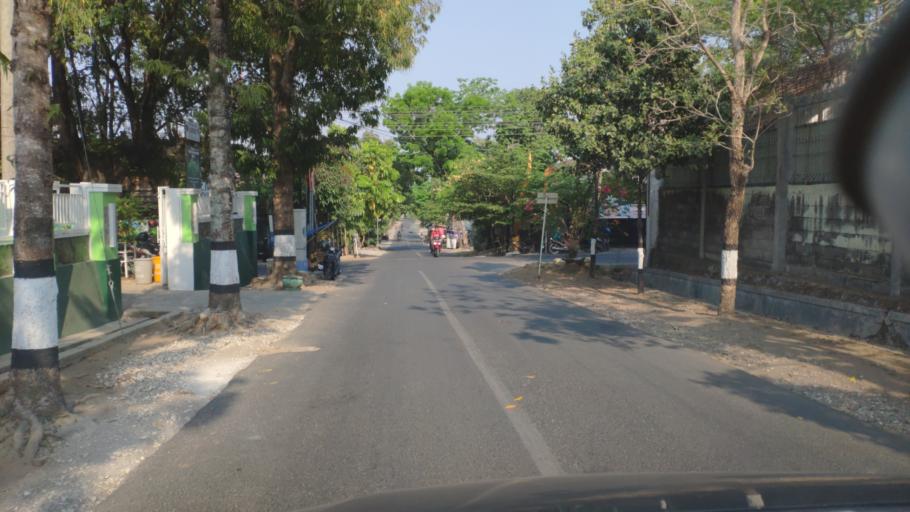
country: ID
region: Central Java
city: Tempelan
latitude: -6.9639
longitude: 111.4145
